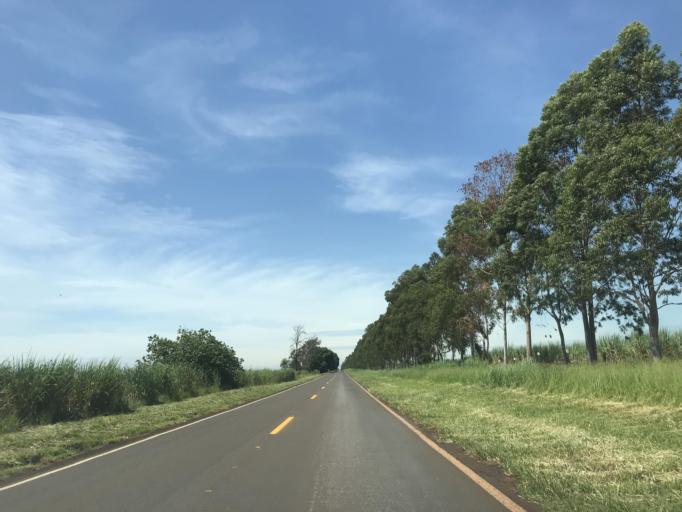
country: BR
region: Parana
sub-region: Paranavai
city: Nova Aurora
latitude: -22.8420
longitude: -52.6569
